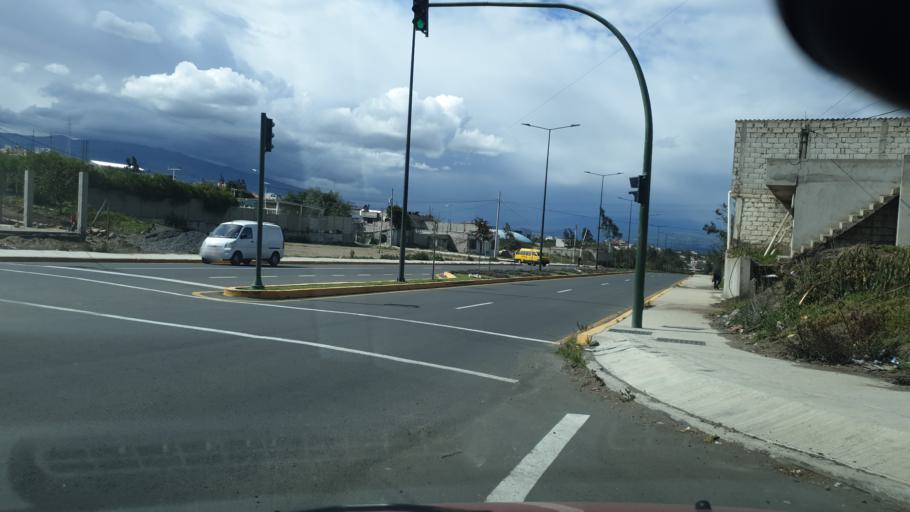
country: EC
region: Tungurahua
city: Ambato
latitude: -1.2939
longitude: -78.6329
